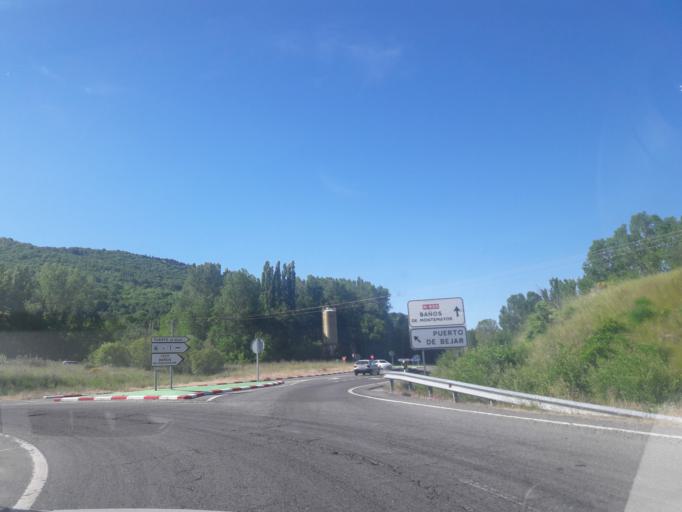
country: ES
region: Castille and Leon
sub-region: Provincia de Salamanca
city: Puerto de Bejar
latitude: 40.3464
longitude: -5.8449
